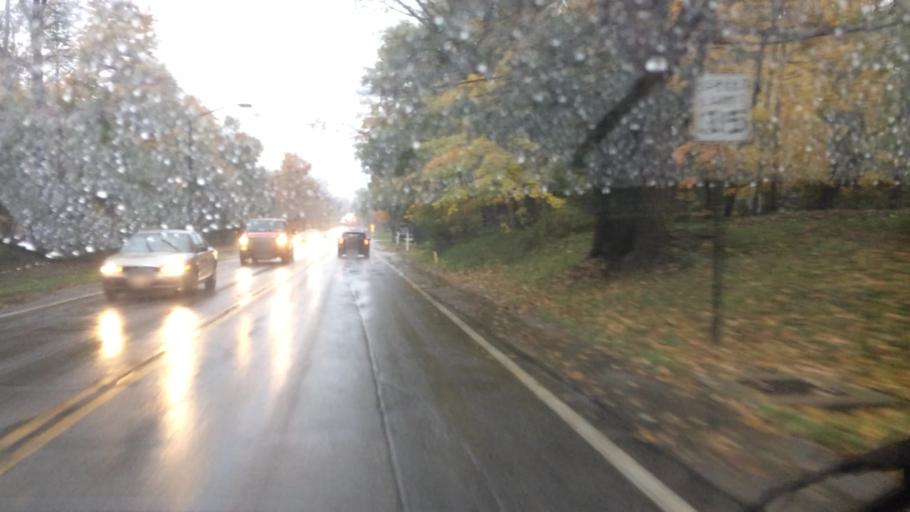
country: US
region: Ohio
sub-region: Summit County
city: Hudson
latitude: 41.2327
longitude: -81.4404
